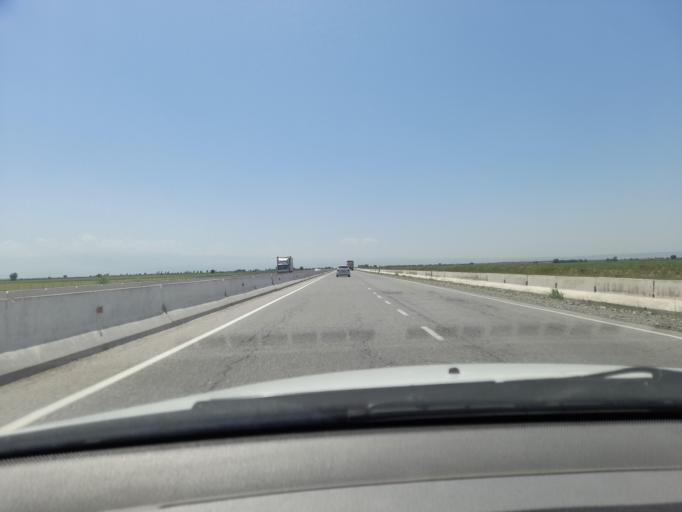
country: UZ
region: Jizzax
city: Paxtakor
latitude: 40.2303
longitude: 67.9988
